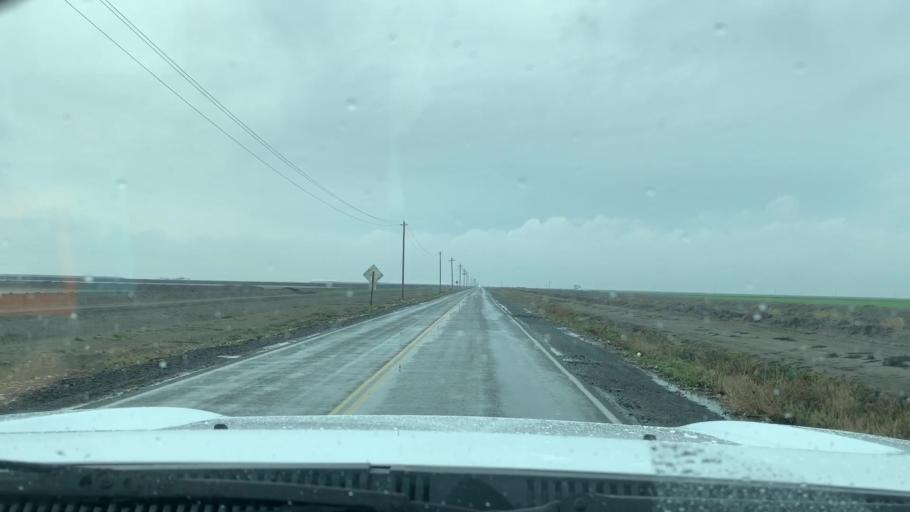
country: US
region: California
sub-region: Tulare County
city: Alpaugh
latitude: 35.9595
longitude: -119.5732
